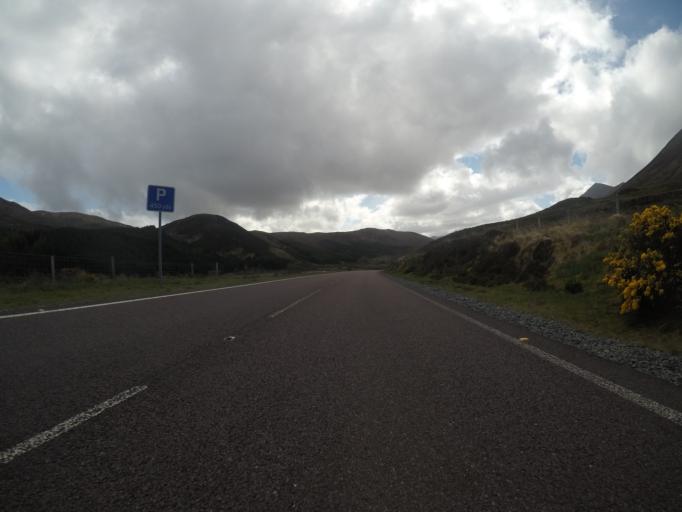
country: GB
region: Scotland
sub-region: Highland
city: Portree
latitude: 57.3062
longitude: -6.0916
